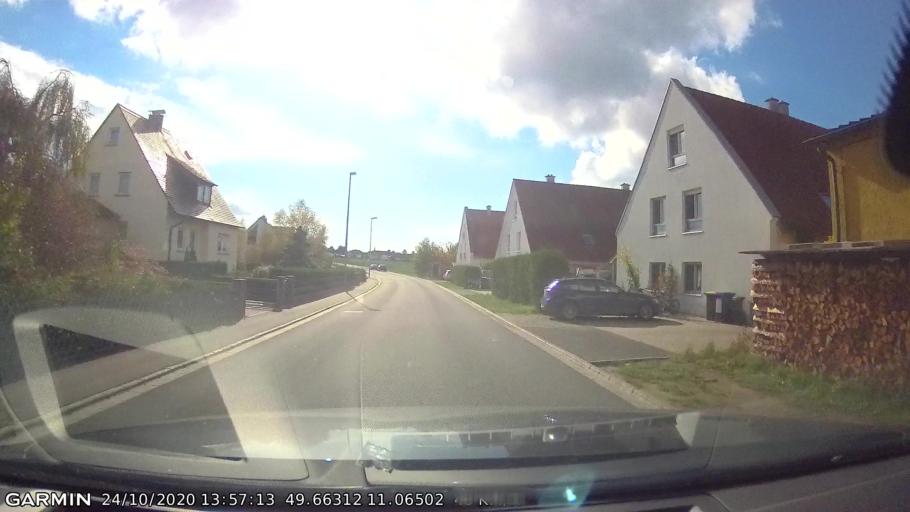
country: DE
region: Bavaria
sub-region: Upper Franconia
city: Poxdorf
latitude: 49.6633
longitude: 11.0649
